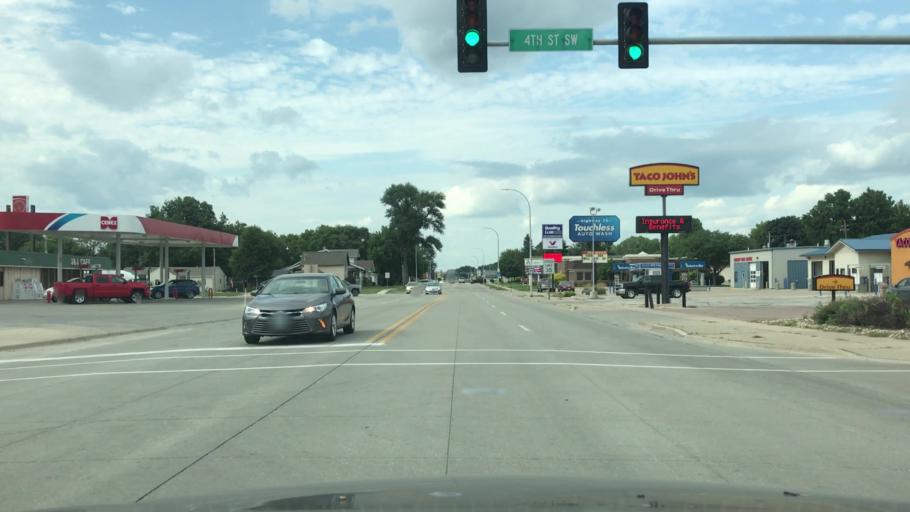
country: US
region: Iowa
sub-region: Plymouth County
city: Le Mars
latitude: 42.7882
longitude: -96.1738
